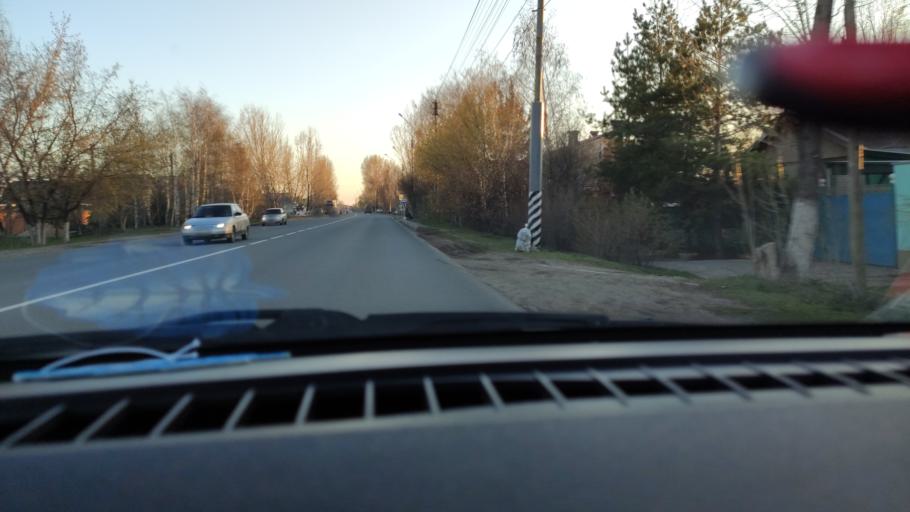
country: RU
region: Saratov
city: Privolzhskiy
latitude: 51.4323
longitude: 46.0563
